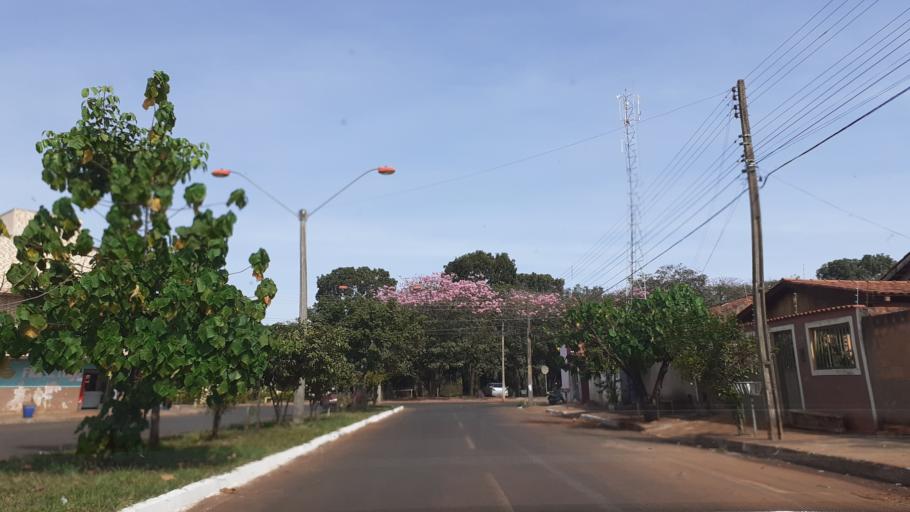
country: BR
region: Goias
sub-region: Itumbiara
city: Itumbiara
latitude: -18.4134
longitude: -49.2577
